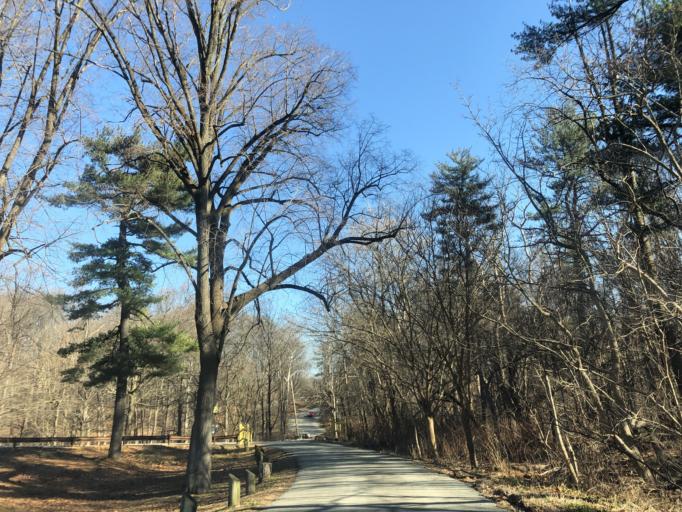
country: US
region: Pennsylvania
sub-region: Montgomery County
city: Bala-Cynwyd
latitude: 39.9957
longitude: -75.2028
